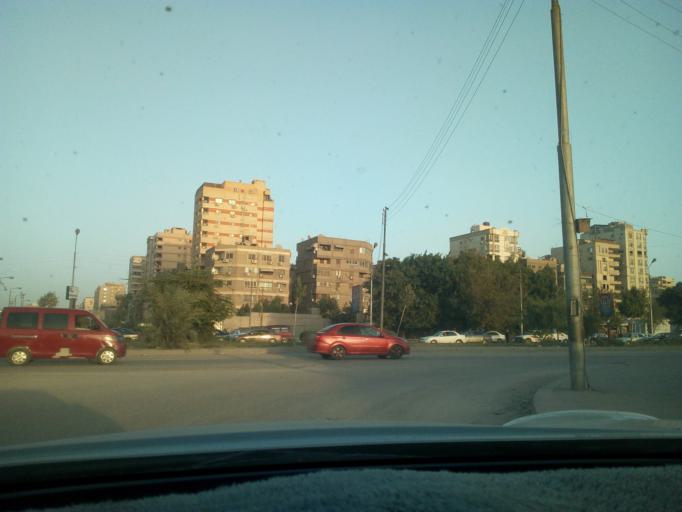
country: EG
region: Muhafazat al Qalyubiyah
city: Al Khankah
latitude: 30.1257
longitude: 31.3626
